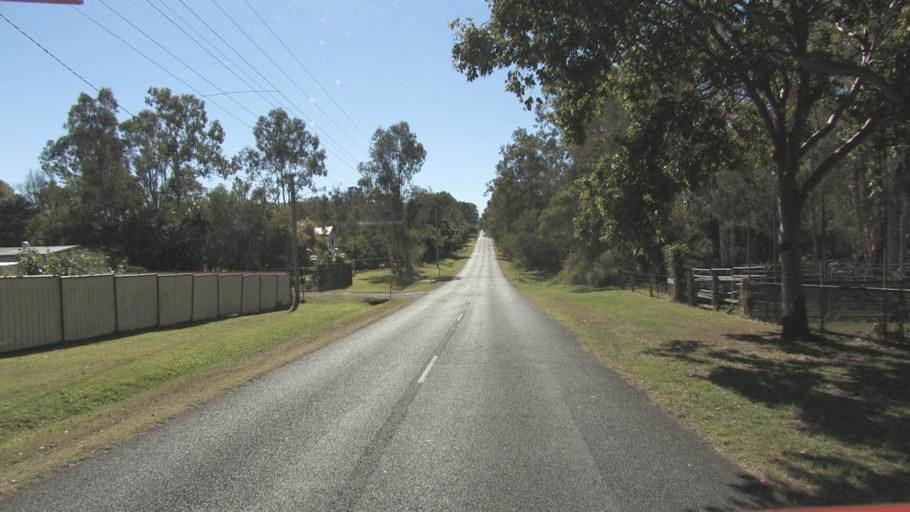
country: AU
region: Queensland
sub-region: Logan
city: Park Ridge South
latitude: -27.7173
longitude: 153.0576
